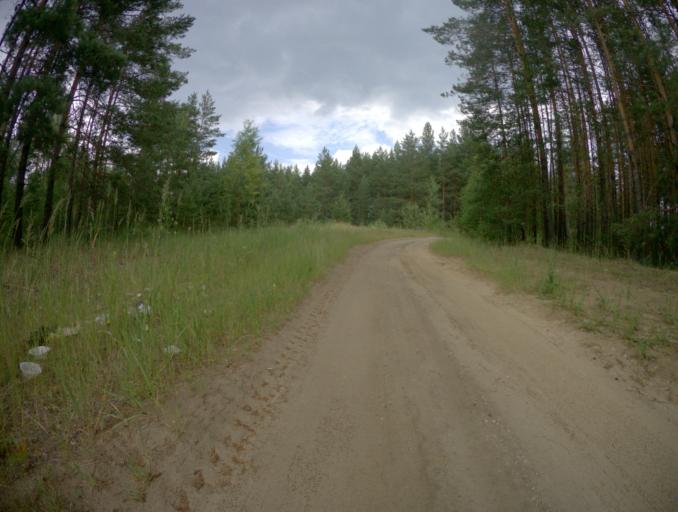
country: RU
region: Nizjnij Novgorod
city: Frolishchi
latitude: 56.3462
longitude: 42.7455
